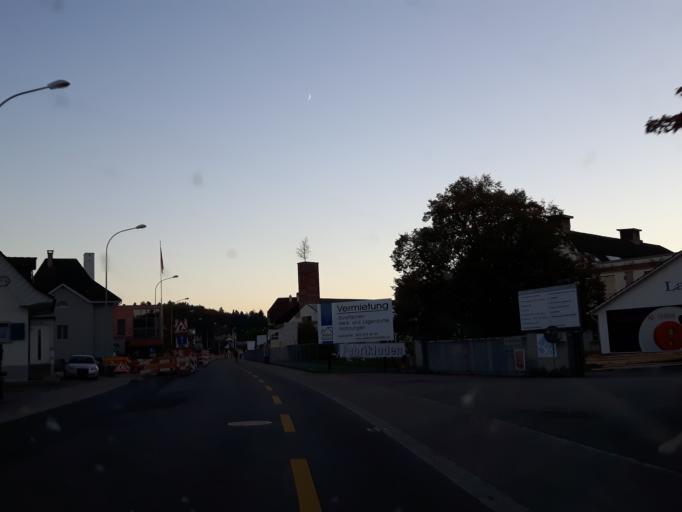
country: CH
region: Bern
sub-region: Oberaargau
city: Lotzwil
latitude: 47.2049
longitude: 7.7828
